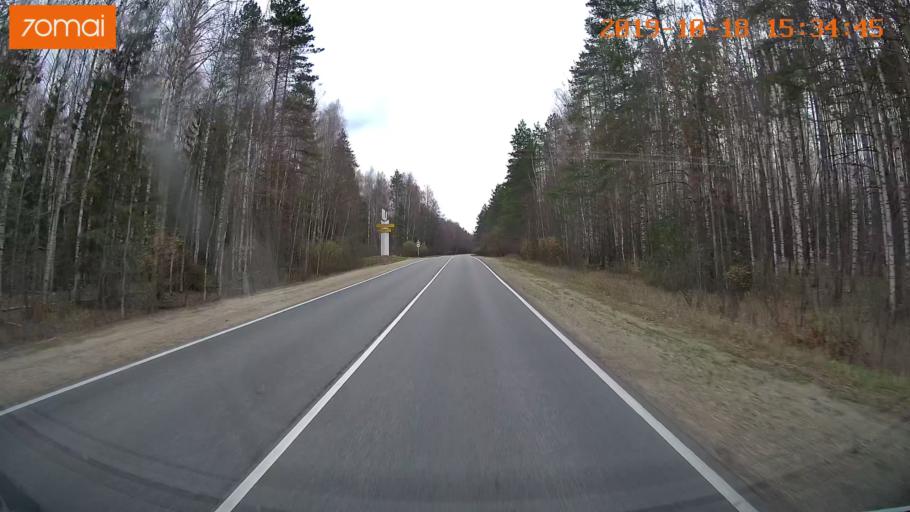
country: RU
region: Vladimir
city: Anopino
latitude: 55.8583
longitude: 40.6382
